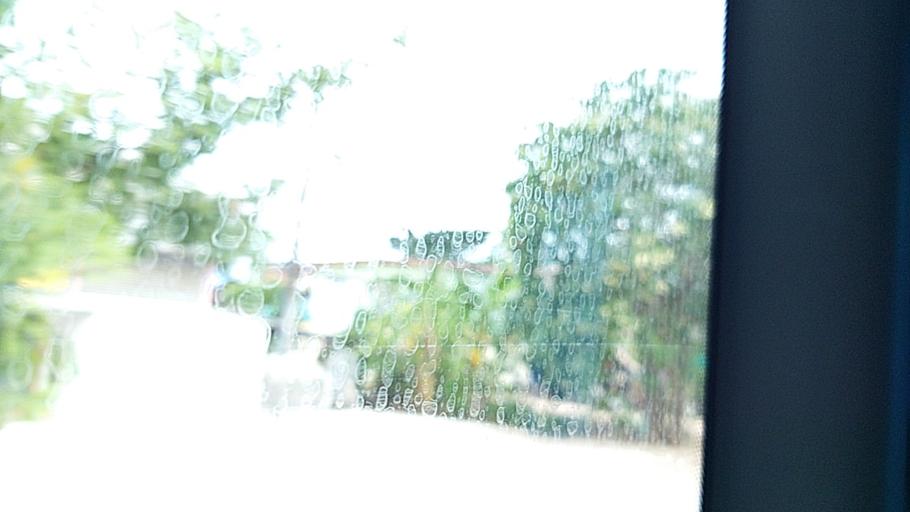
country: TH
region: Maha Sarakham
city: Maha Sarakham
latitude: 16.1485
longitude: 103.3989
